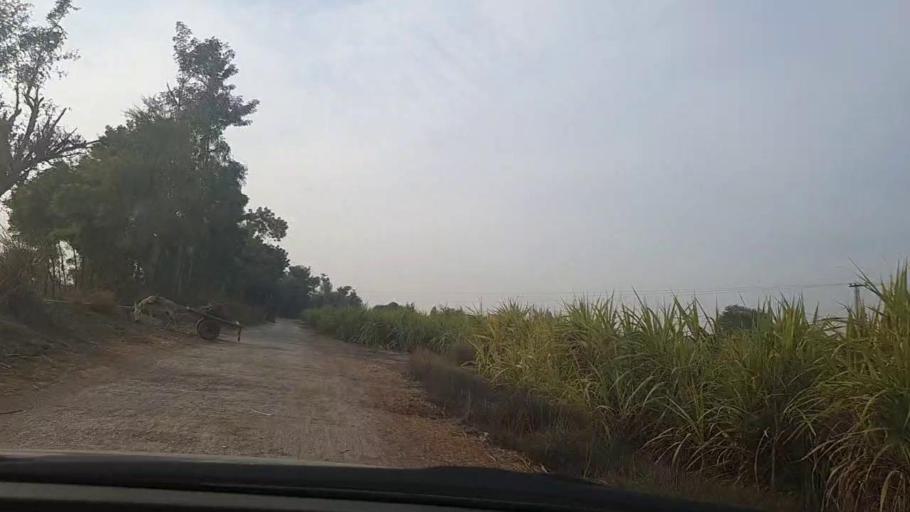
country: PK
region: Sindh
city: Daulatpur
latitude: 26.3345
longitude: 68.0406
